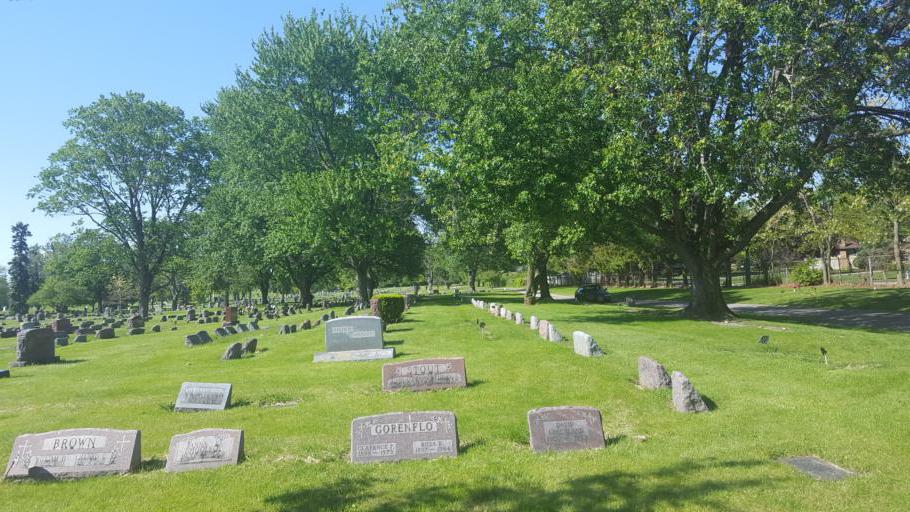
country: US
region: Ohio
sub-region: Marion County
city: Marion
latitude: 40.5746
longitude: -83.1191
